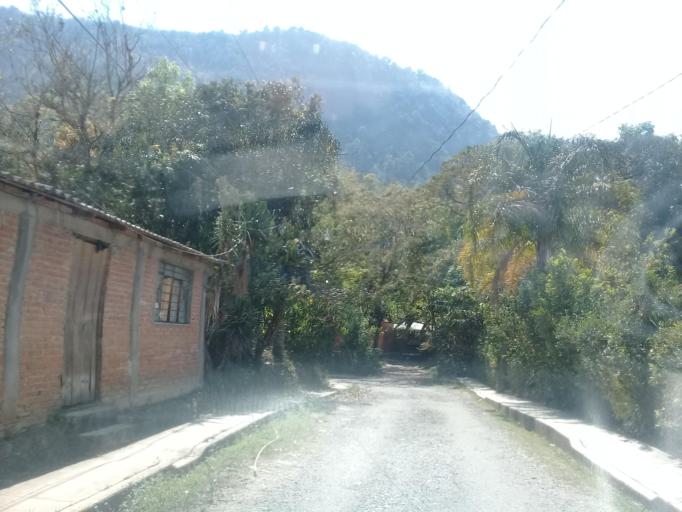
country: MX
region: Veracruz
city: Jalapilla
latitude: 18.8045
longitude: -97.0725
